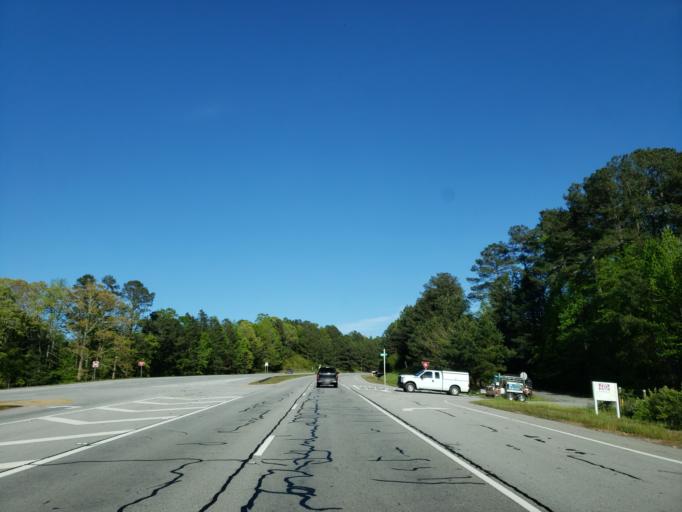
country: US
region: Georgia
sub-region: Paulding County
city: Dallas
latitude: 33.9185
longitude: -84.8690
